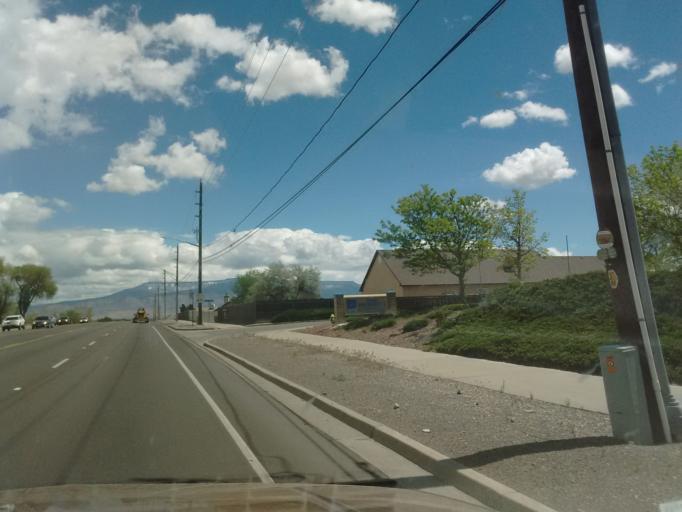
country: US
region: Colorado
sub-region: Mesa County
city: Fruitvale
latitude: 39.0917
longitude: -108.5275
